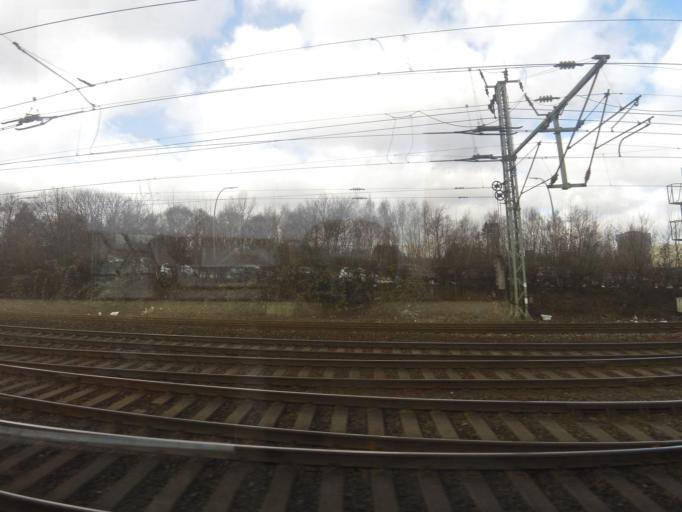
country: DE
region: Hamburg
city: Harburg
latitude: 53.4603
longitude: 9.9920
